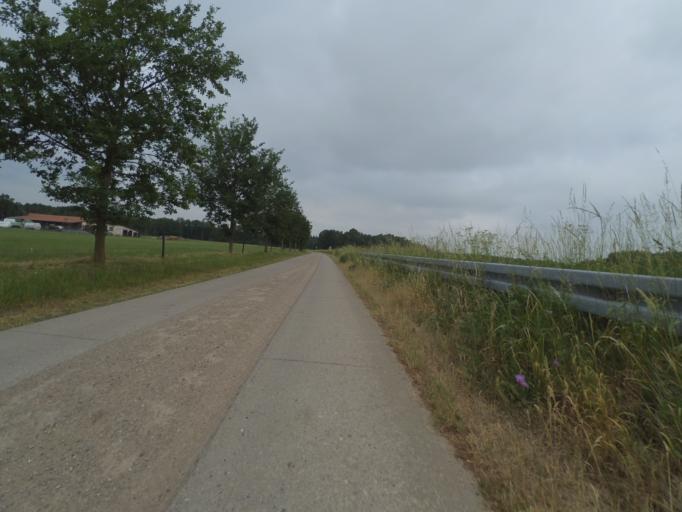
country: DE
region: Mecklenburg-Vorpommern
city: Goldberg
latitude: 53.5155
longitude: 12.0843
